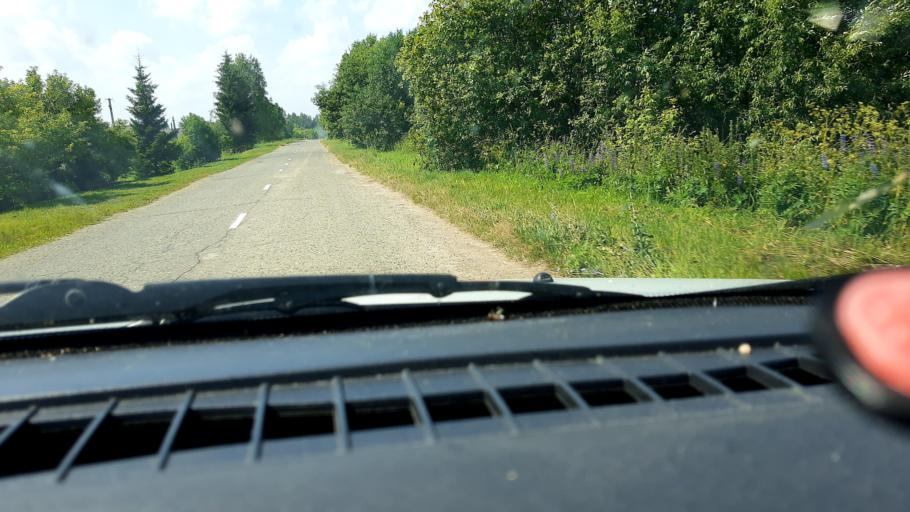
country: RU
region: Nizjnij Novgorod
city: Sharanga
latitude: 57.0530
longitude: 46.5567
